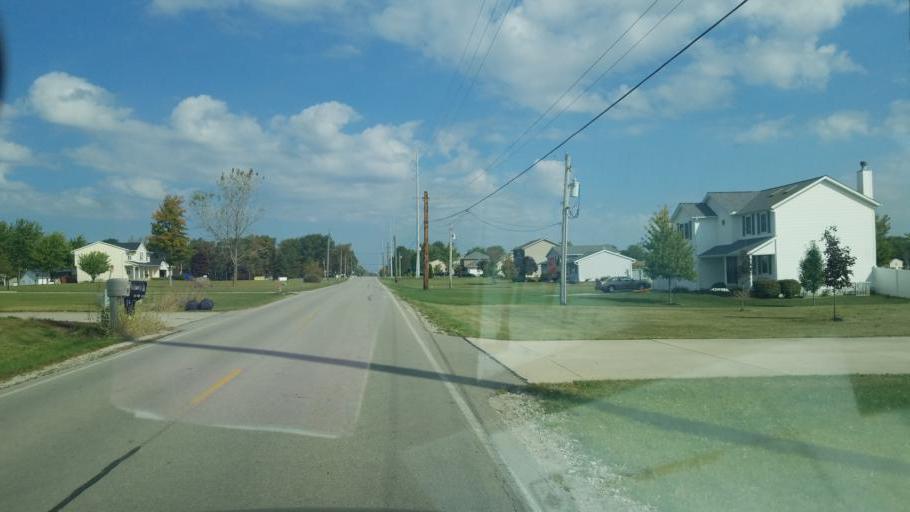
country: US
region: Ohio
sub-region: Marion County
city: Marion
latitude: 40.5315
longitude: -83.1507
